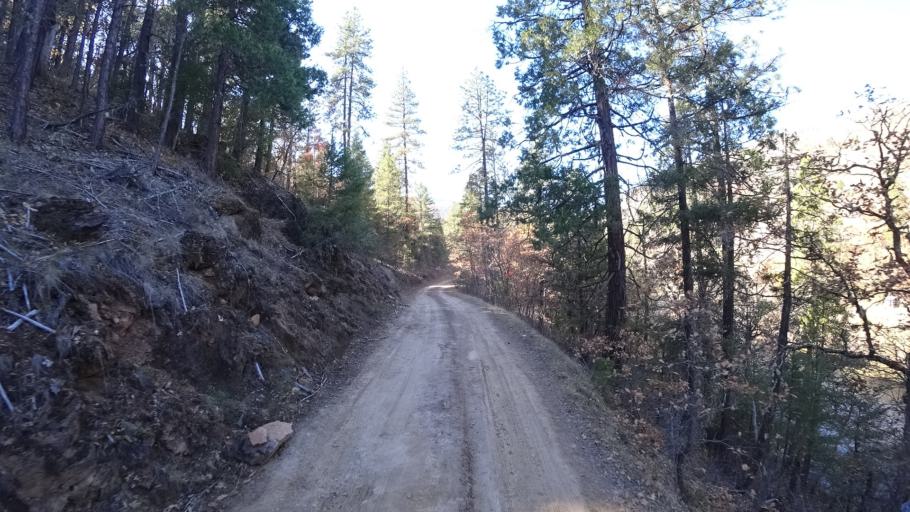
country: US
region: California
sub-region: Siskiyou County
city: Yreka
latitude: 41.8578
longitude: -122.7496
